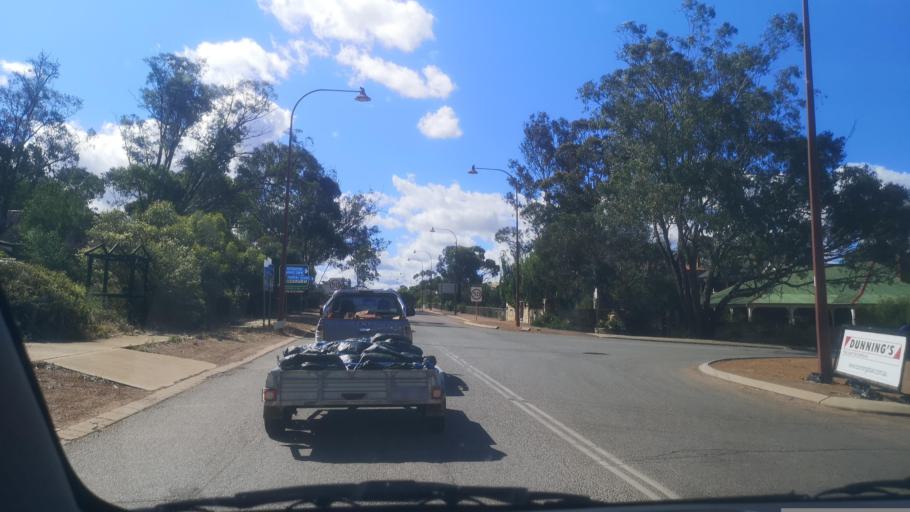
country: AU
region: Western Australia
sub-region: Toodyay
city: Toodyay
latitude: -31.5557
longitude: 116.4754
